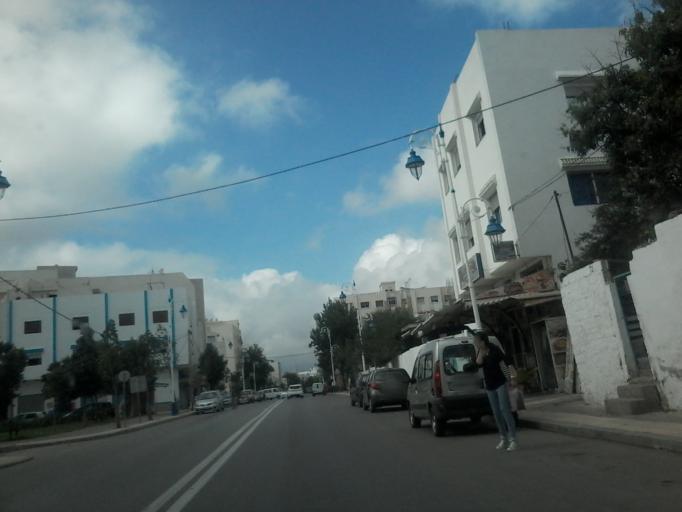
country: MA
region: Tanger-Tetouan
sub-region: Tetouan
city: Martil
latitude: 35.6261
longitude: -5.2769
